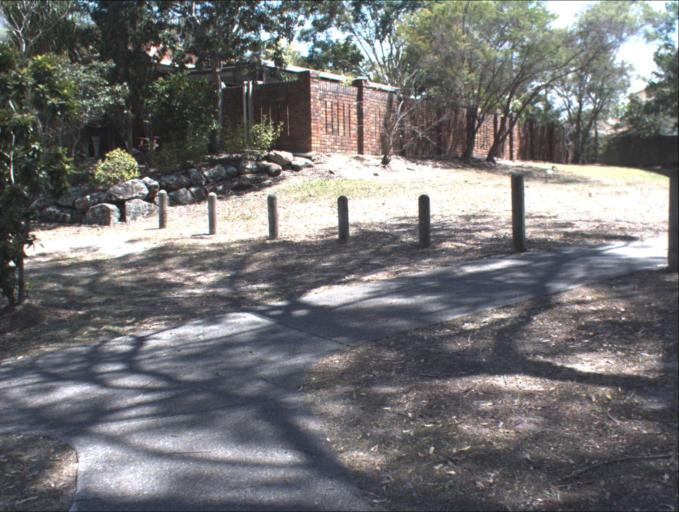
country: AU
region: Queensland
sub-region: Logan
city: Rochedale South
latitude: -27.5910
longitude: 153.1333
